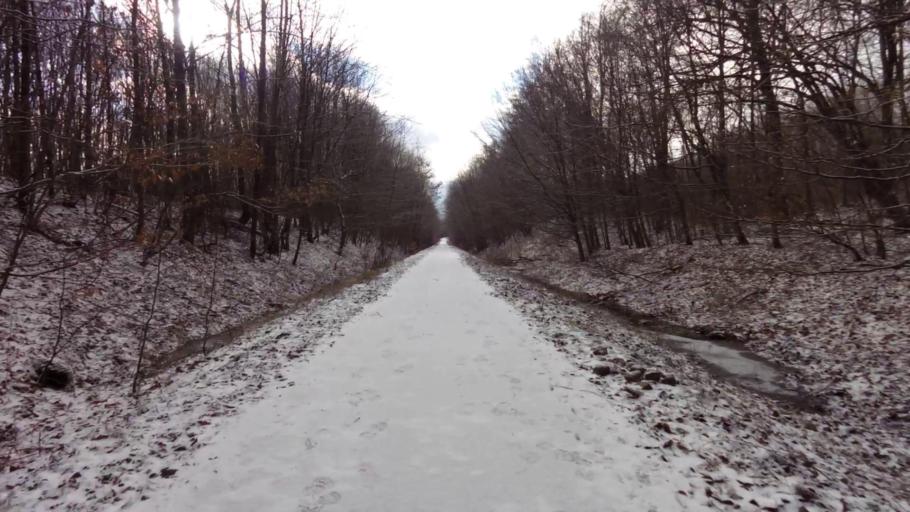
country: PL
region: West Pomeranian Voivodeship
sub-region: Powiat swidwinski
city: Polczyn-Zdroj
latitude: 53.7413
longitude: 16.0544
